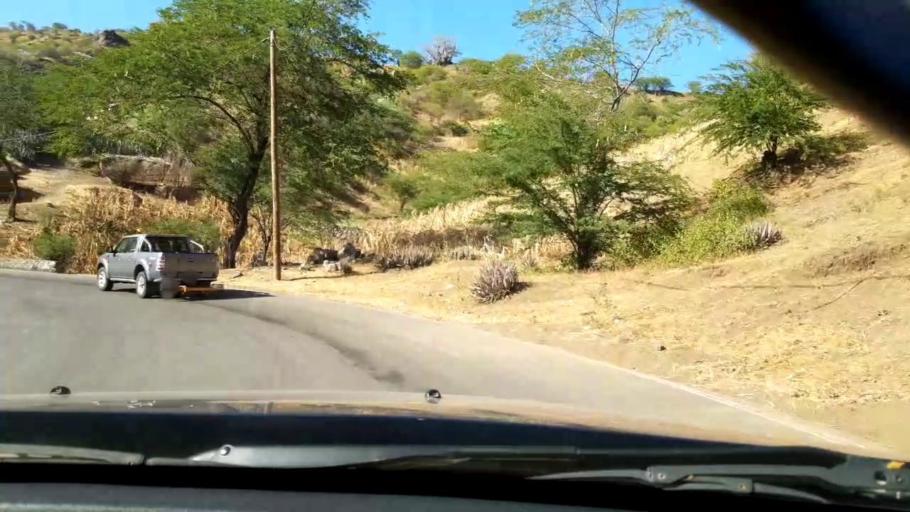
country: CV
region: Sao Lourenco dos Orgaos
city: Joao Teves
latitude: 15.0729
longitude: -23.5665
